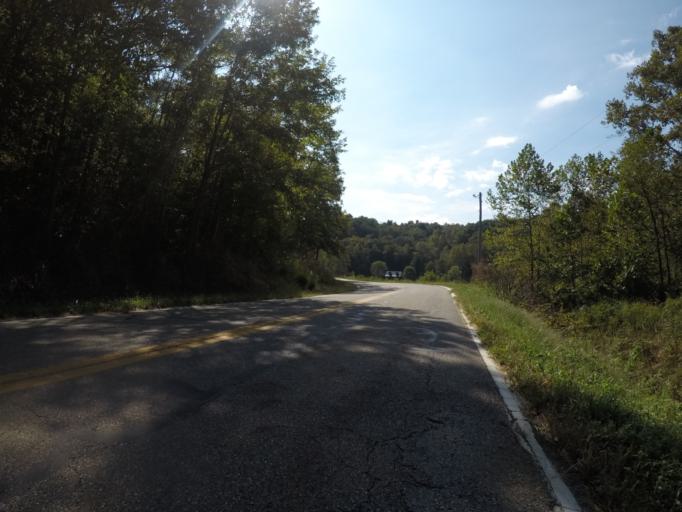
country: US
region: West Virginia
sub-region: Cabell County
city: Lesage
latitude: 38.6371
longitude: -82.4317
